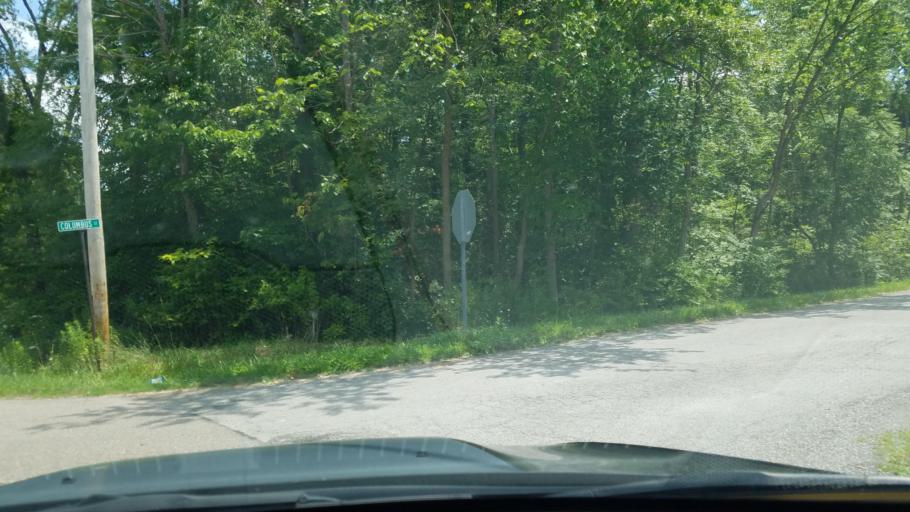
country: US
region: Ohio
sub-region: Trumbull County
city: Bolindale
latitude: 41.2031
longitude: -80.7760
